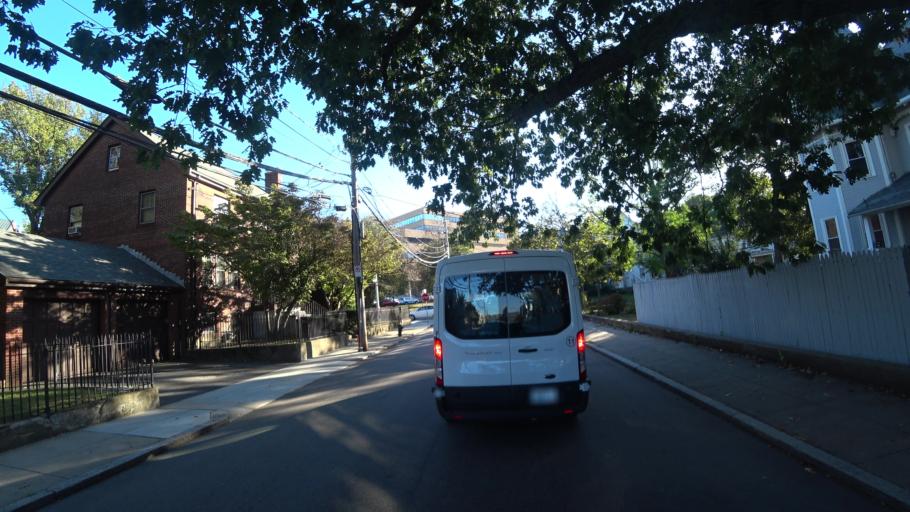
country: US
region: Massachusetts
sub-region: Norfolk County
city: Brookline
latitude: 42.3507
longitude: -71.1477
